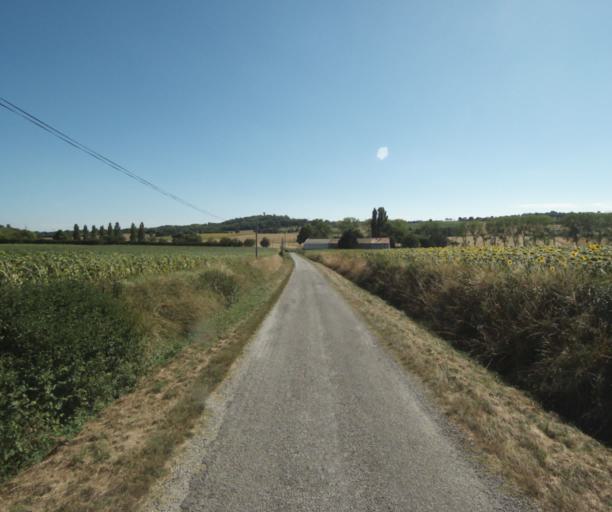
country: FR
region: Midi-Pyrenees
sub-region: Departement de la Haute-Garonne
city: Saint-Felix-Lauragais
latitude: 43.5052
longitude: 1.9031
